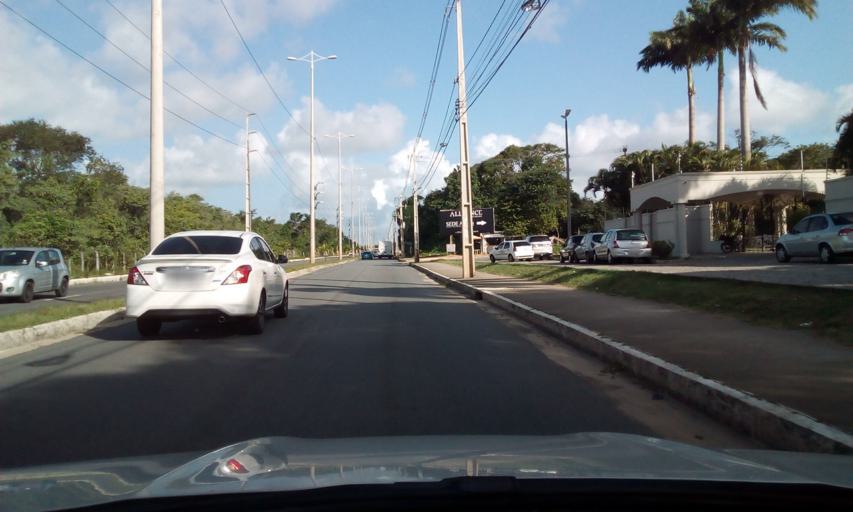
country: BR
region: Paraiba
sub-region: Joao Pessoa
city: Joao Pessoa
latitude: -7.1352
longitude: -34.8226
